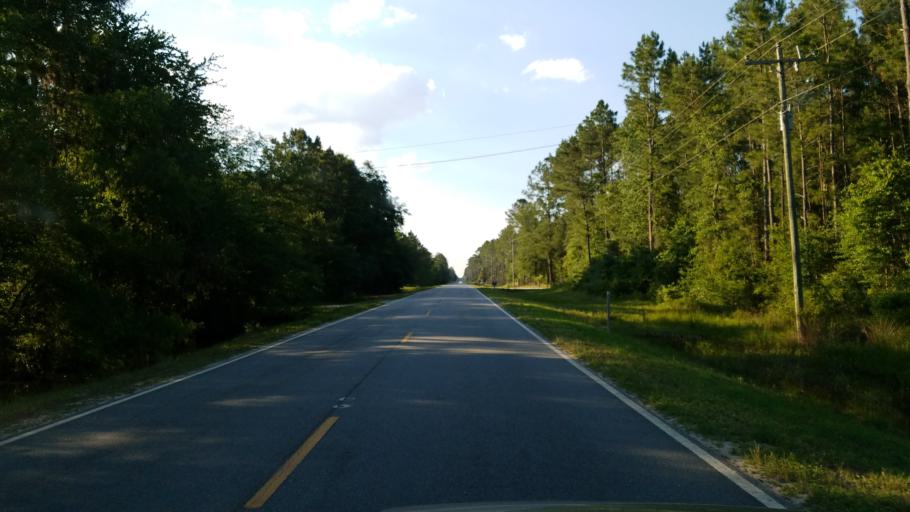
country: US
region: Georgia
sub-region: Lanier County
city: Lakeland
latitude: 31.0804
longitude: -83.0752
